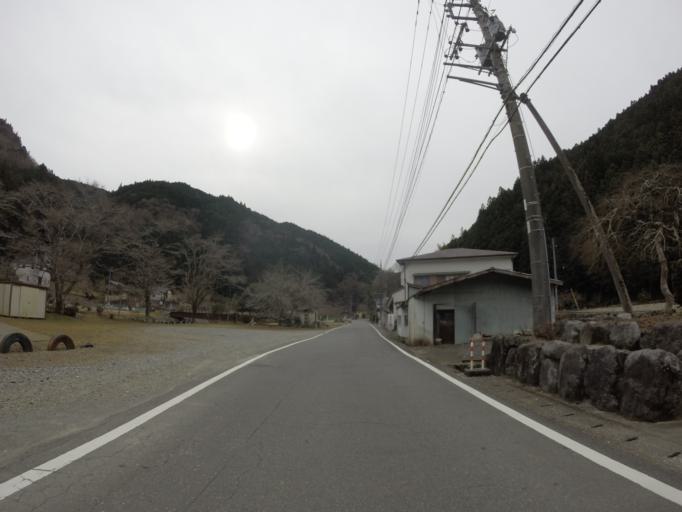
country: JP
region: Shizuoka
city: Fujinomiya
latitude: 35.2530
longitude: 138.5328
